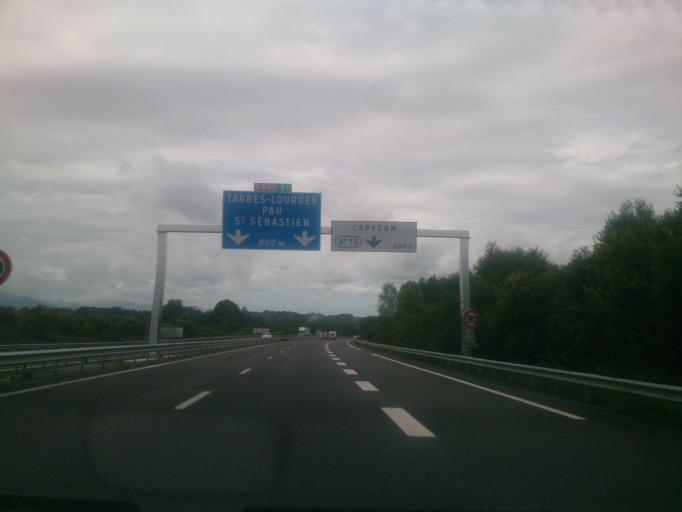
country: FR
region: Midi-Pyrenees
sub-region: Departement des Hautes-Pyrenees
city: Capvern
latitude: 43.0994
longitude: 0.3487
